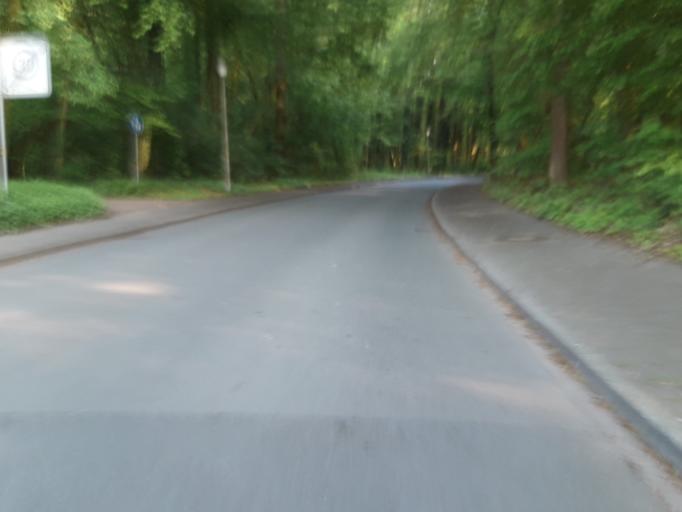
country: DE
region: North Rhine-Westphalia
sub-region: Regierungsbezirk Munster
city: Muenster
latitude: 51.9084
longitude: 7.6558
